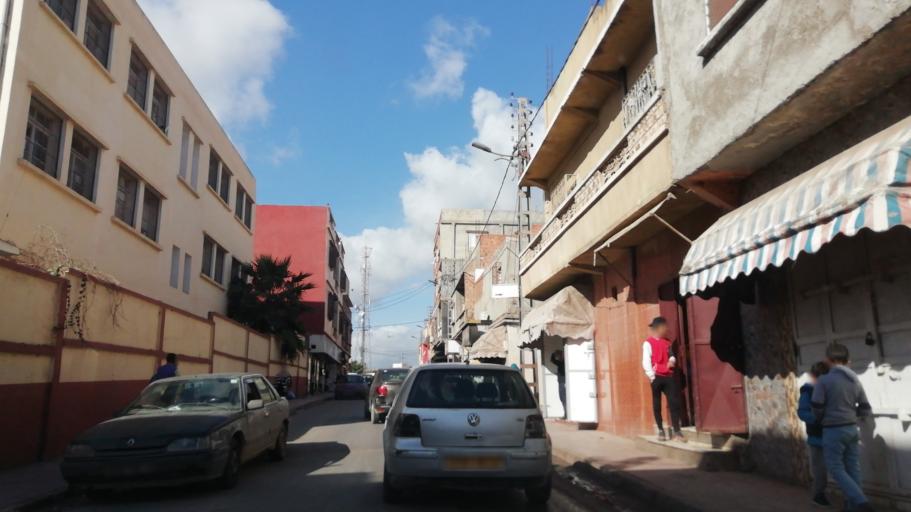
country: DZ
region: Oran
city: Es Senia
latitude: 35.6390
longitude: -0.6661
